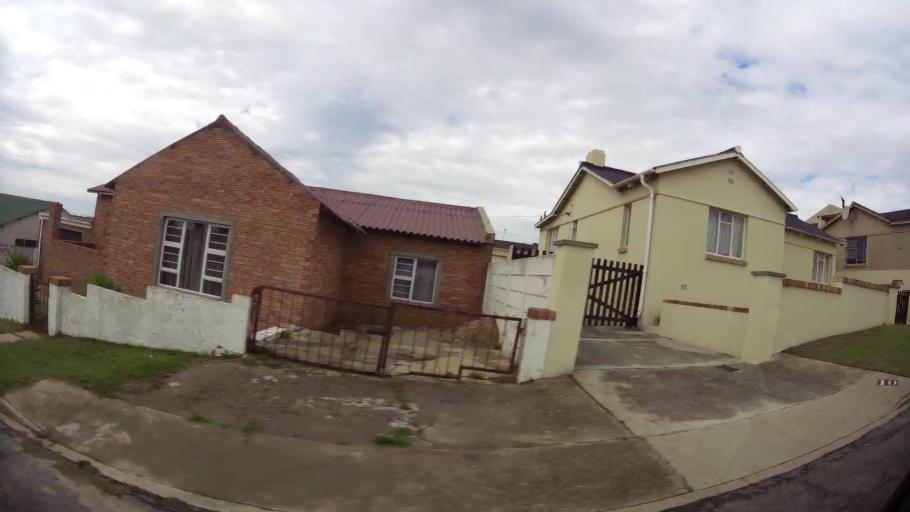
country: ZA
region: Eastern Cape
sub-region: Nelson Mandela Bay Metropolitan Municipality
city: Port Elizabeth
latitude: -33.9386
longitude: 25.5855
